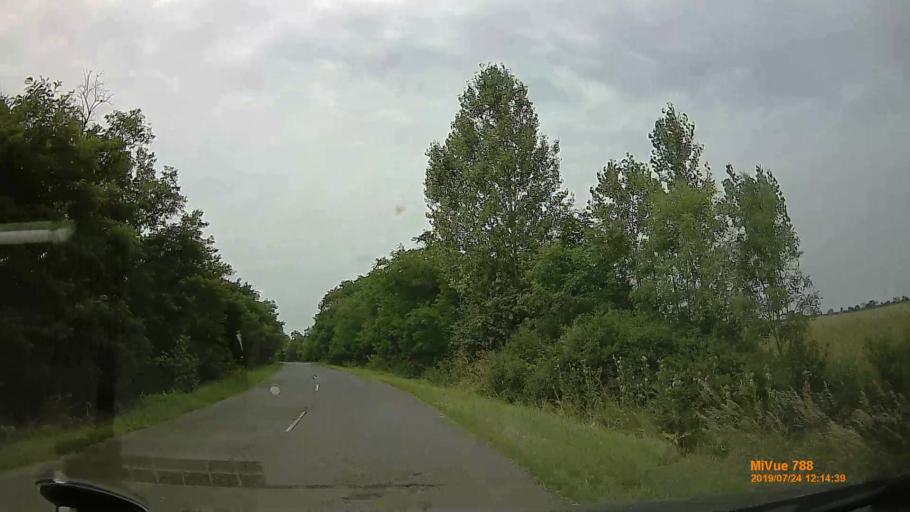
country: HU
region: Szabolcs-Szatmar-Bereg
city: Vasarosnameny
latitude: 48.1888
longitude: 22.3483
